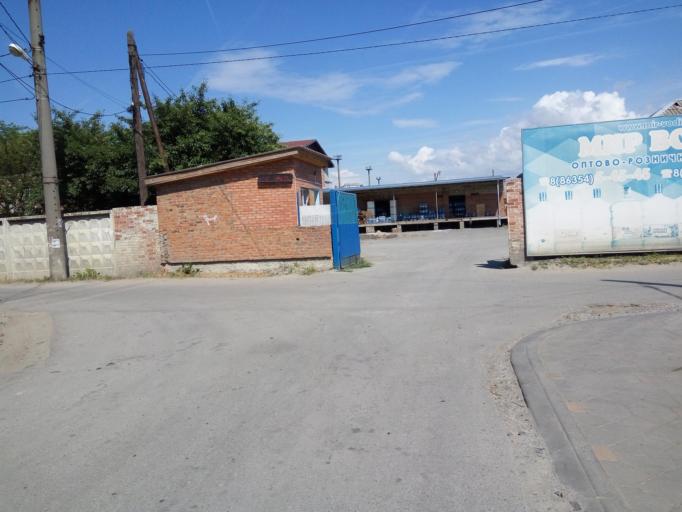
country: RU
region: Rostov
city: Bataysk
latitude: 47.1341
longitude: 39.7532
